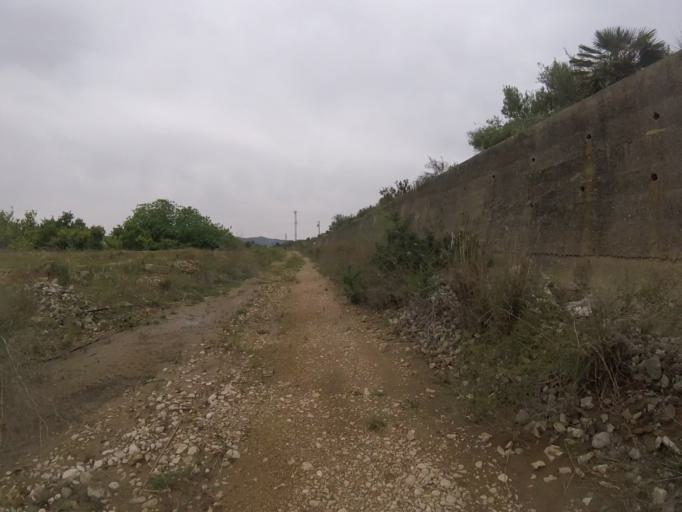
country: ES
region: Valencia
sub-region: Provincia de Castello
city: Alcoceber
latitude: 40.2625
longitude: 0.2576
